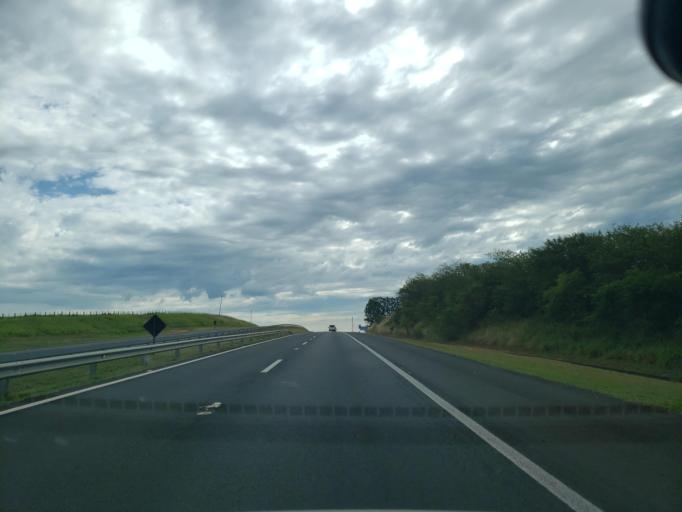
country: BR
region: Sao Paulo
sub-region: Bauru
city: Bauru
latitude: -22.1944
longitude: -49.2016
